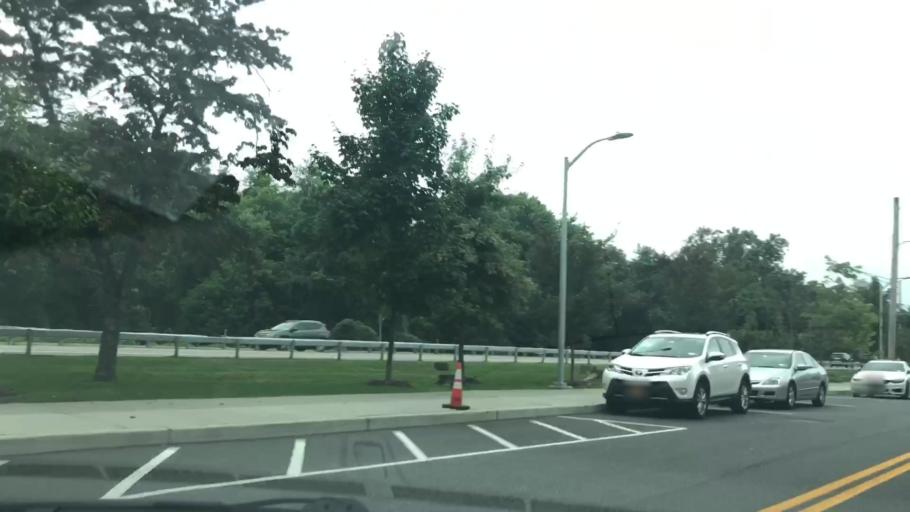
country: US
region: New York
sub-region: Westchester County
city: Ardsley
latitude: 41.0044
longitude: -73.8557
